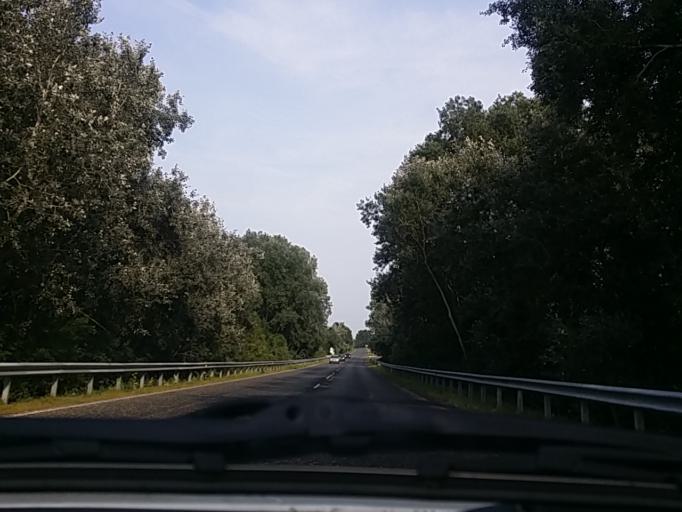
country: HU
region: Fejer
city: Bicske
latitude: 47.4949
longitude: 18.6870
